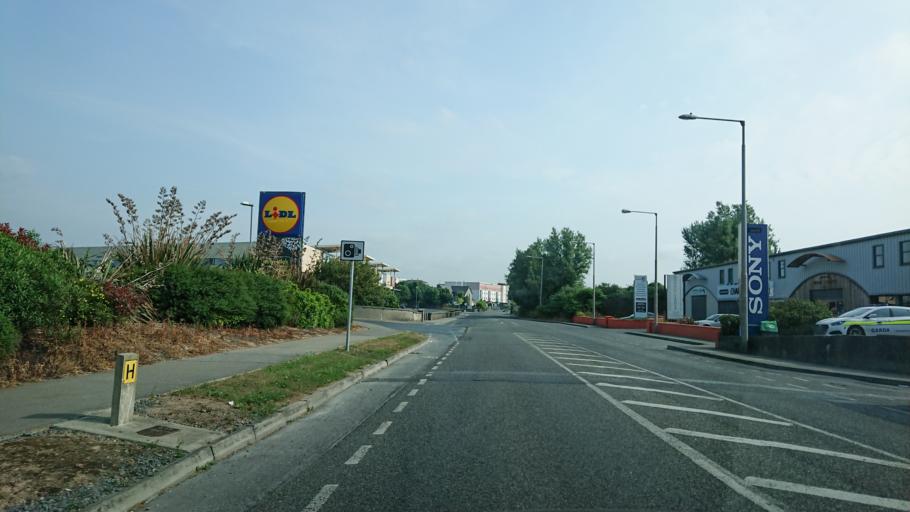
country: IE
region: Munster
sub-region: Waterford
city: Waterford
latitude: 52.2485
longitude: -7.1189
